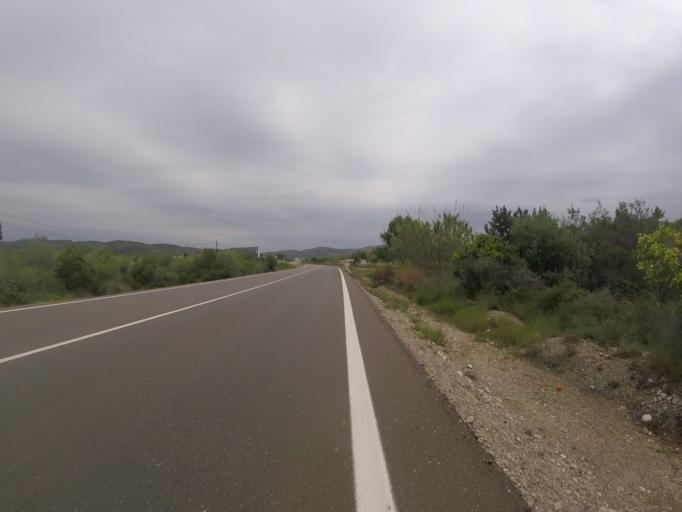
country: ES
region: Valencia
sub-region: Provincia de Castello
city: Alcoceber
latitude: 40.2539
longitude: 0.2459
